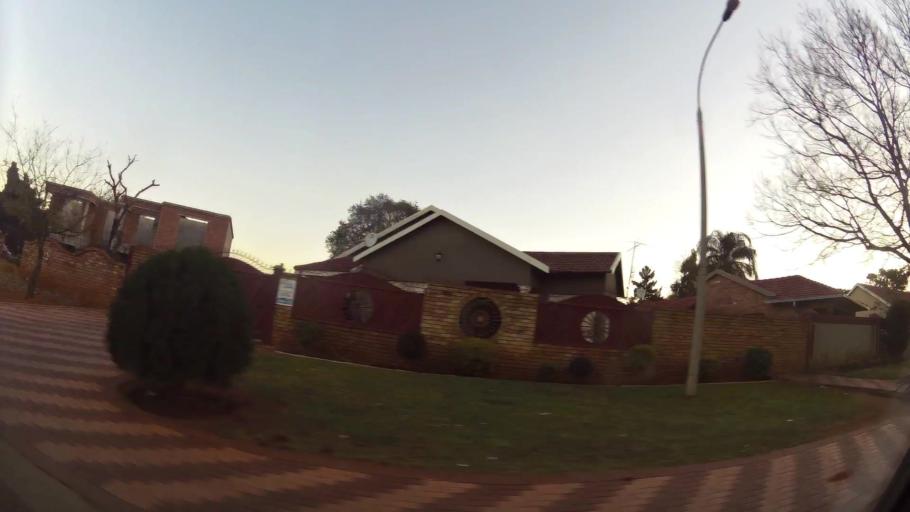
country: ZA
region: North-West
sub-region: Bojanala Platinum District Municipality
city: Rustenburg
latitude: -25.6606
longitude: 27.2165
